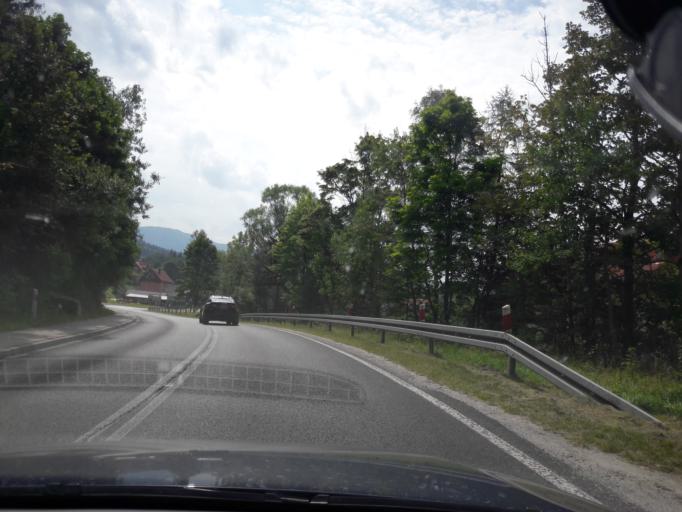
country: PL
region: Lesser Poland Voivodeship
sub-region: Powiat suski
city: Zawoja
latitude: 49.6468
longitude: 19.5439
